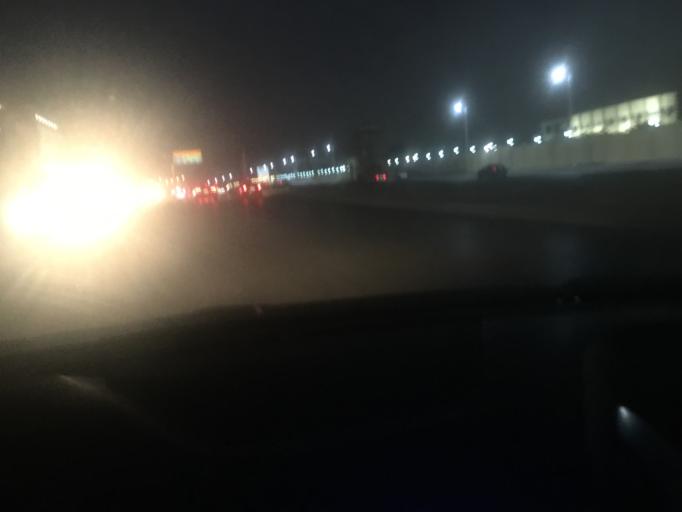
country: EG
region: Muhafazat al Qahirah
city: Cairo
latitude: 30.0791
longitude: 31.3713
